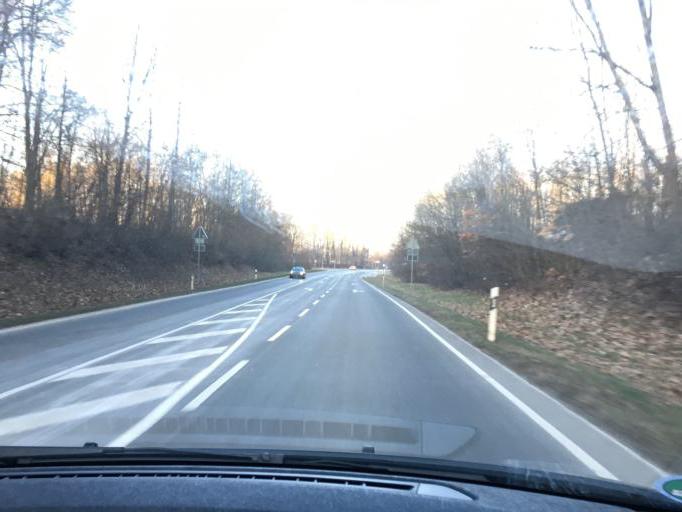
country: DE
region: North Rhine-Westphalia
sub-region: Regierungsbezirk Koln
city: Niederzier
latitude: 50.9081
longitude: 6.4408
